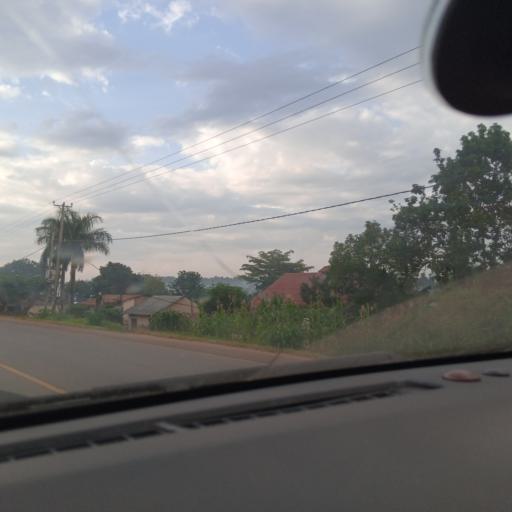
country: UG
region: Central Region
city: Masaka
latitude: -0.3375
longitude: 31.6990
